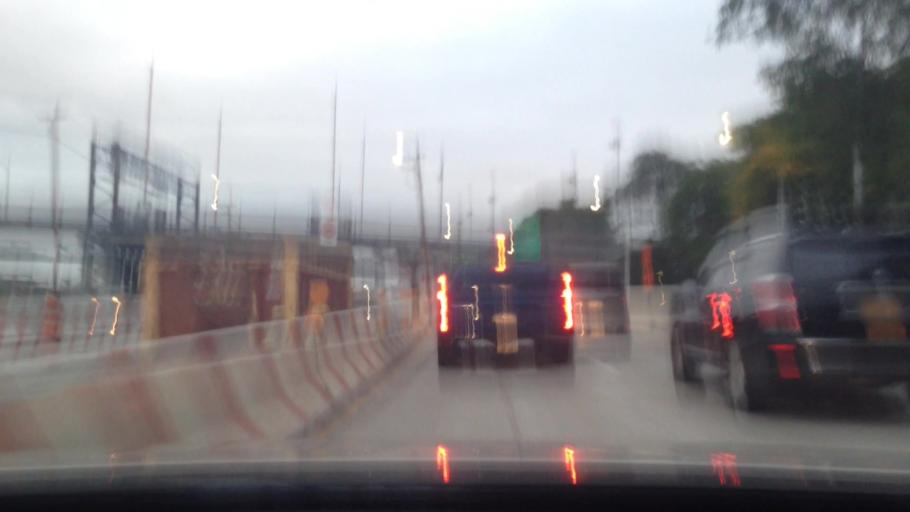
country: US
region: New York
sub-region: New York County
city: Manhattan
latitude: 40.8078
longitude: -73.9344
